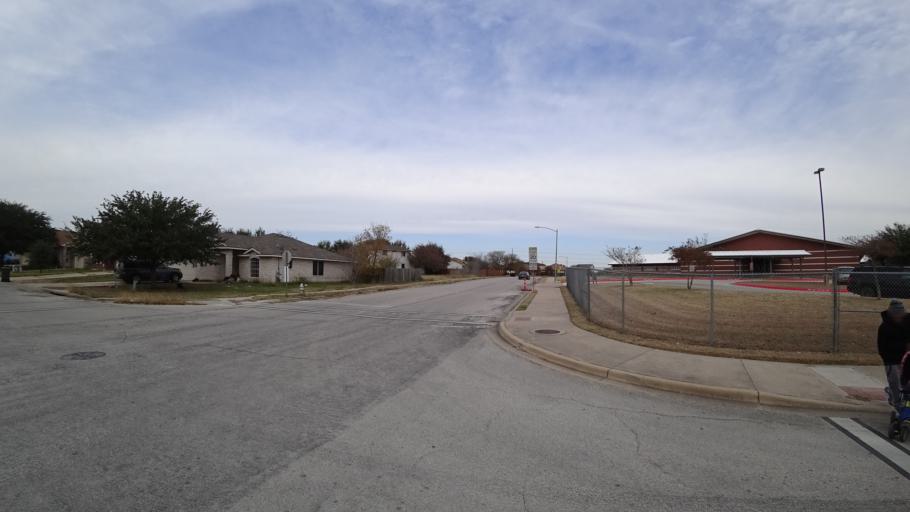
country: US
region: Texas
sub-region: Travis County
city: Garfield
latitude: 30.1565
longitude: -97.6452
